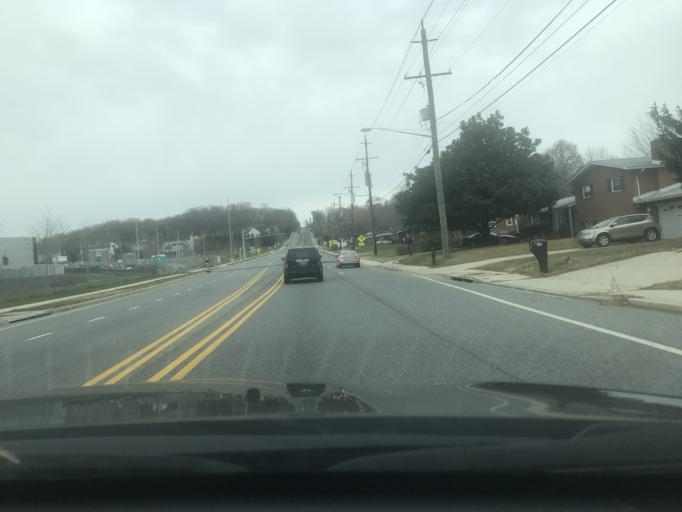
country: US
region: Maryland
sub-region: Prince George's County
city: Oxon Hill
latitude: 38.7913
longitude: -76.9721
